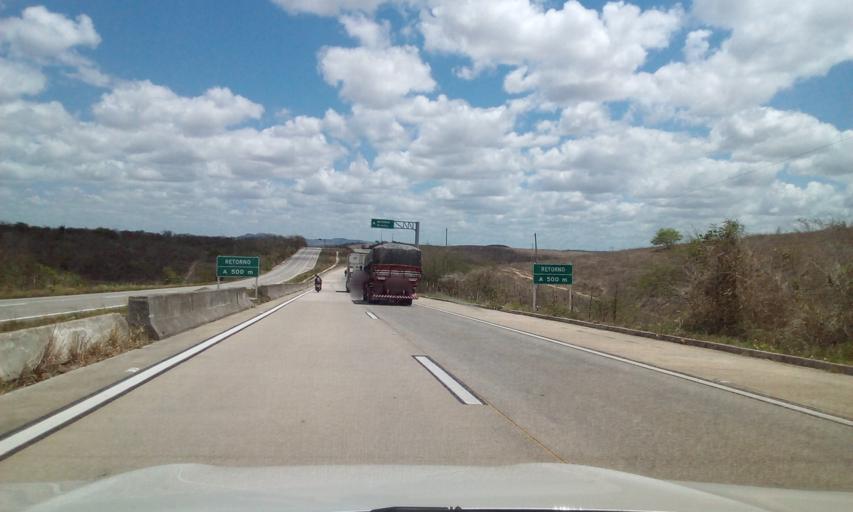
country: BR
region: Alagoas
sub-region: Porto Real Do Colegio
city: Porto Real do Colegio
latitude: -10.1664
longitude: -36.8189
